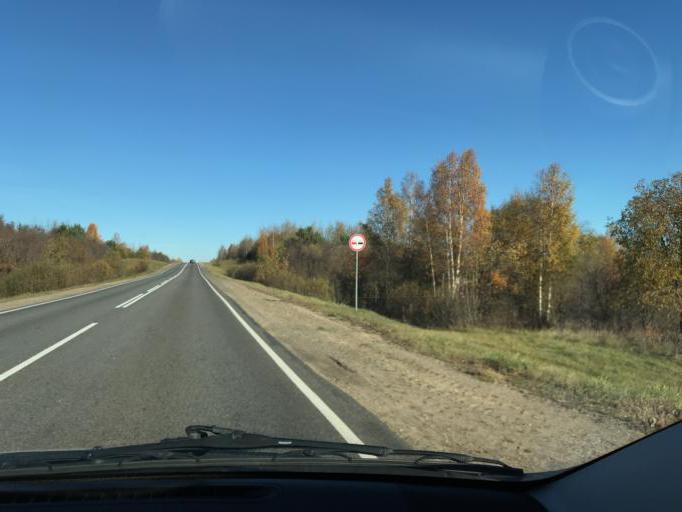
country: BY
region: Vitebsk
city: Lyepyel'
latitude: 55.0210
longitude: 28.7432
